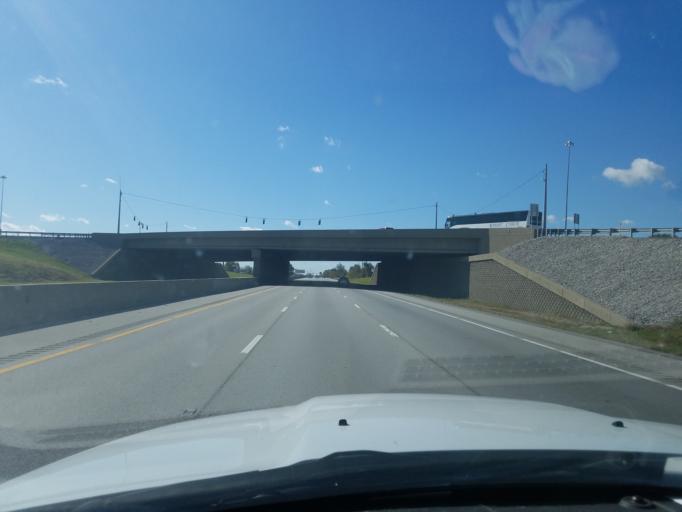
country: US
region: Kentucky
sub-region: Warren County
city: Plano
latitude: 36.9358
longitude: -86.4175
